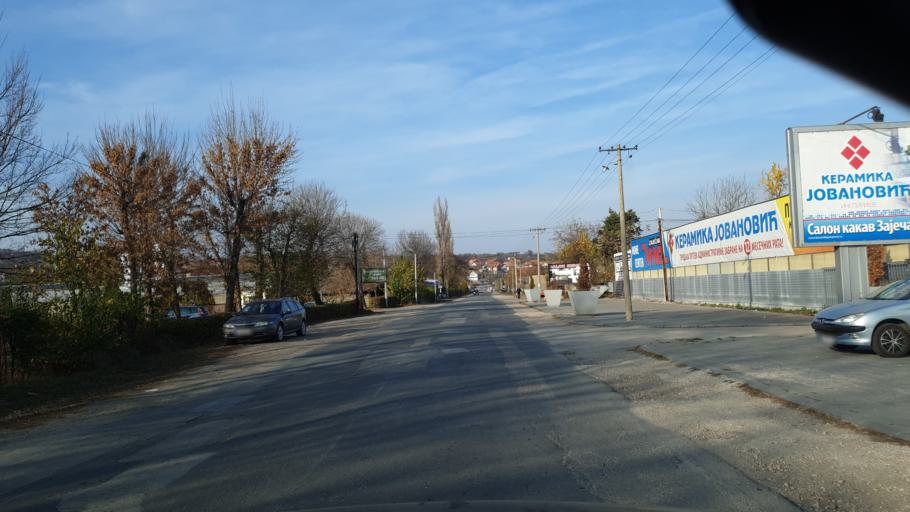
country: RS
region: Central Serbia
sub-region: Zajecarski Okrug
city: Zajecar
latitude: 43.9139
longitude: 22.2907
